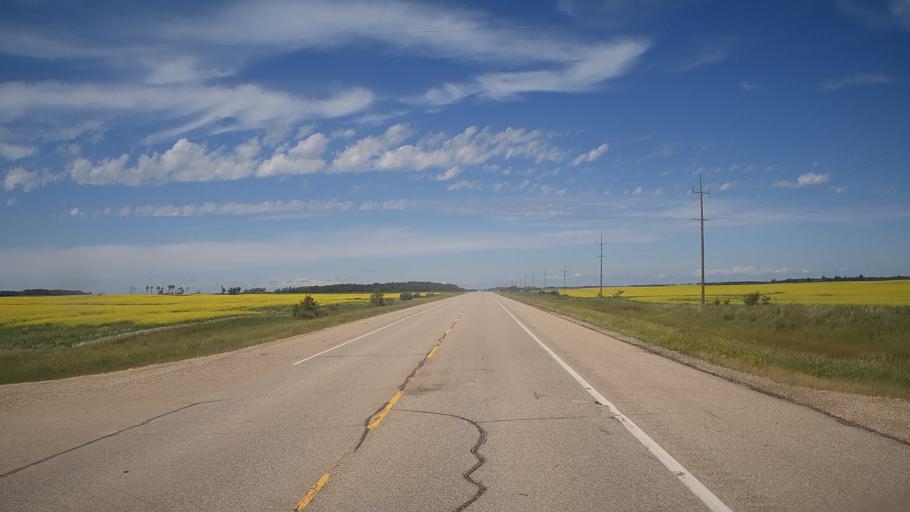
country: CA
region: Saskatchewan
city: Langenburg
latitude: 50.6679
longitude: -101.2761
